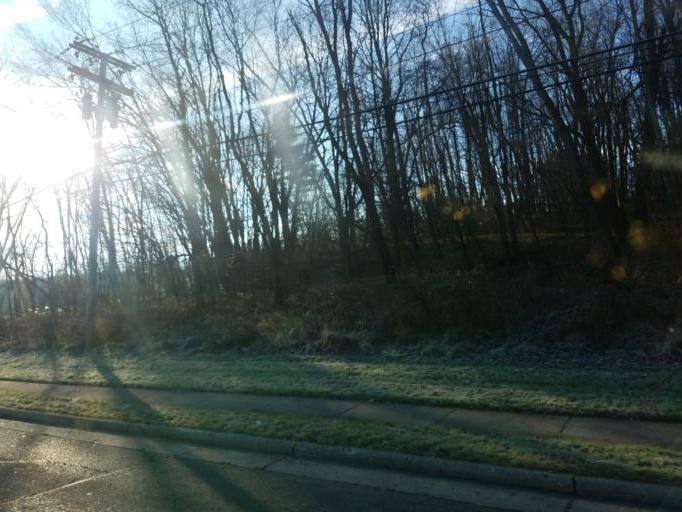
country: US
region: Ohio
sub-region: Knox County
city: Mount Vernon
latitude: 40.3971
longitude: -82.4524
